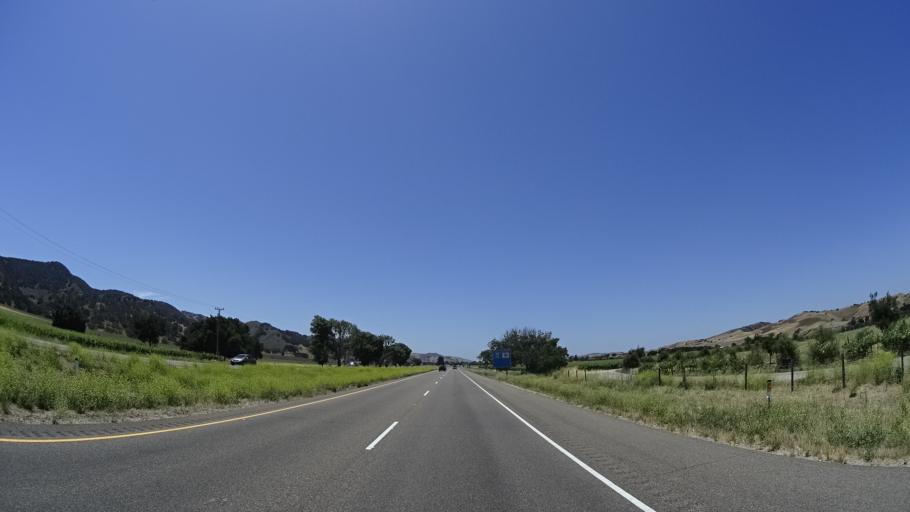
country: US
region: California
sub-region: Santa Barbara County
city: Los Alamos
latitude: 34.7377
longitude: -120.2565
